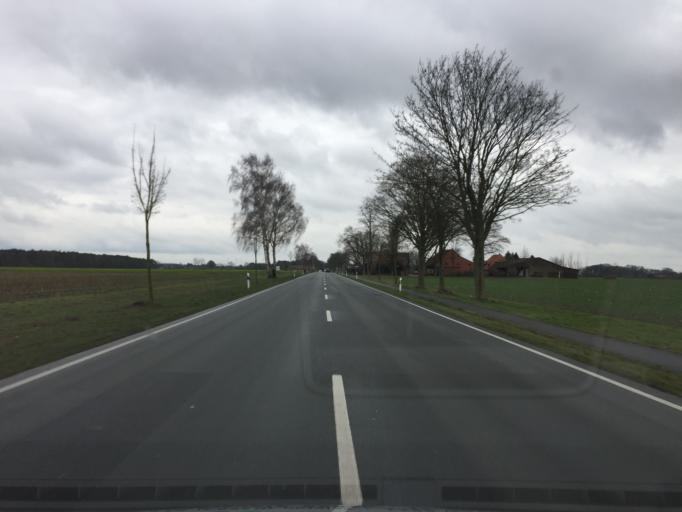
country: DE
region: Lower Saxony
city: Scholen
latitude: 52.7109
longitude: 8.7736
